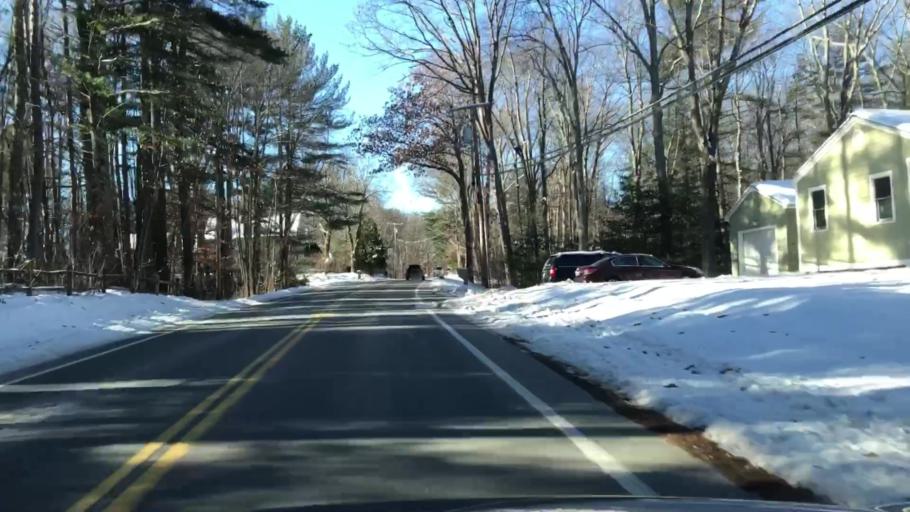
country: US
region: New Hampshire
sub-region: Hillsborough County
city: Bedford
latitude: 42.9277
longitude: -71.5640
